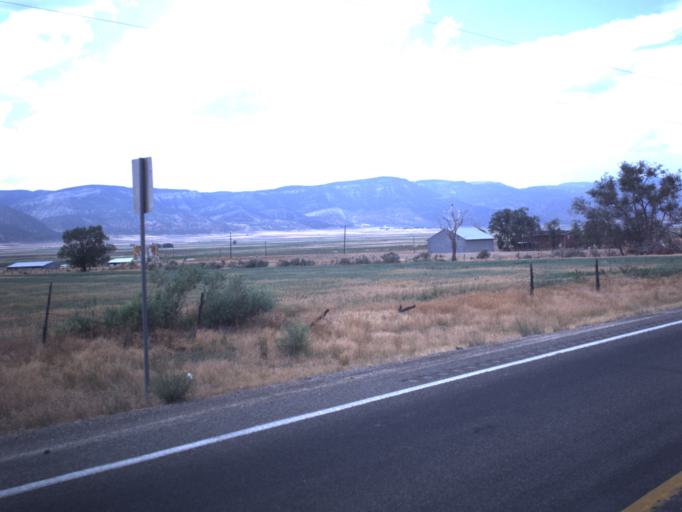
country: US
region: Utah
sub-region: Sanpete County
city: Ephraim
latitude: 39.4240
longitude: -111.5621
